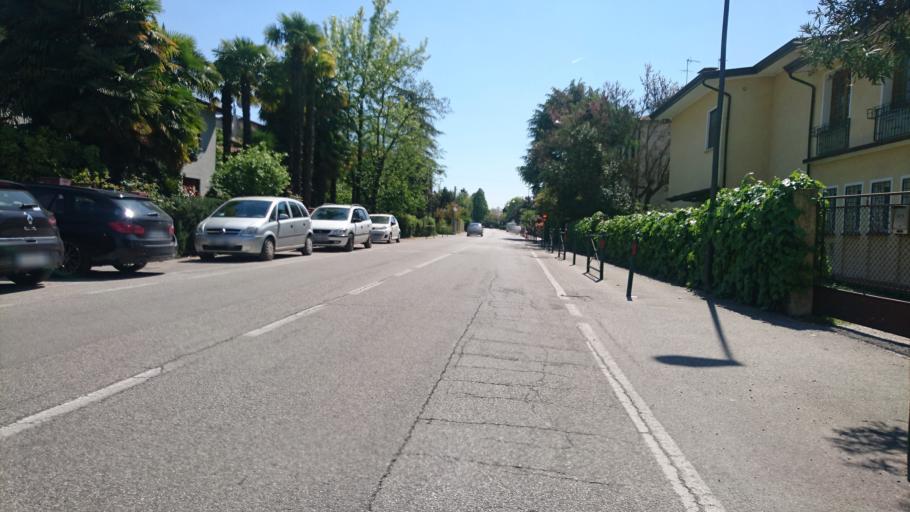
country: IT
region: Veneto
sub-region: Provincia di Treviso
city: Dosson
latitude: 45.6576
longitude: 12.2568
